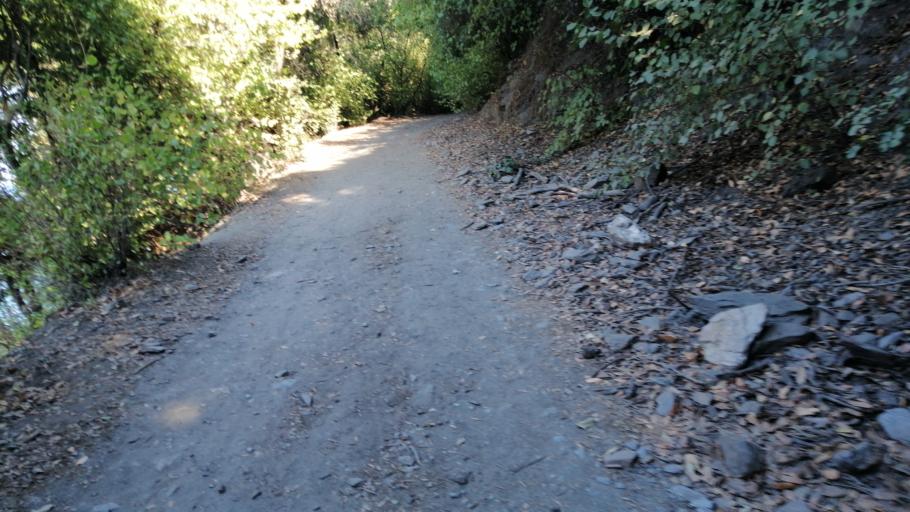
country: TR
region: Aydin
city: Atburgazi
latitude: 37.6902
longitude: 27.1341
